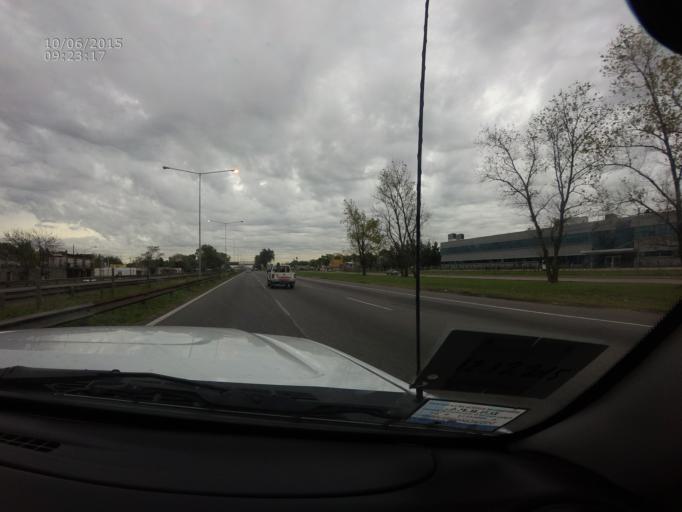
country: AR
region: Buenos Aires
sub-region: Partido de Campana
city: Campana
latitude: -34.2070
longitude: -58.9323
